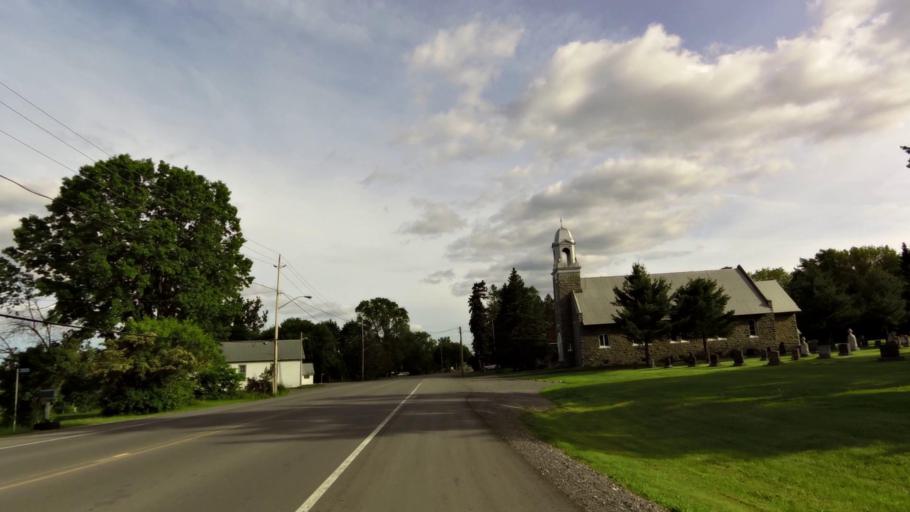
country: CA
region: Ontario
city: Ottawa
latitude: 45.1998
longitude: -75.5681
